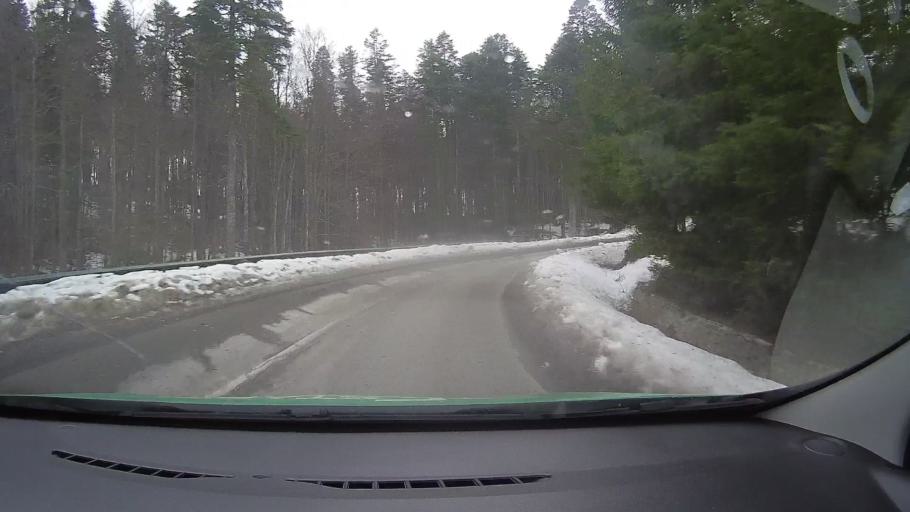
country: RO
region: Prahova
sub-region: Oras Sinaia
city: Sinaia
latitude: 45.3511
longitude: 25.5382
